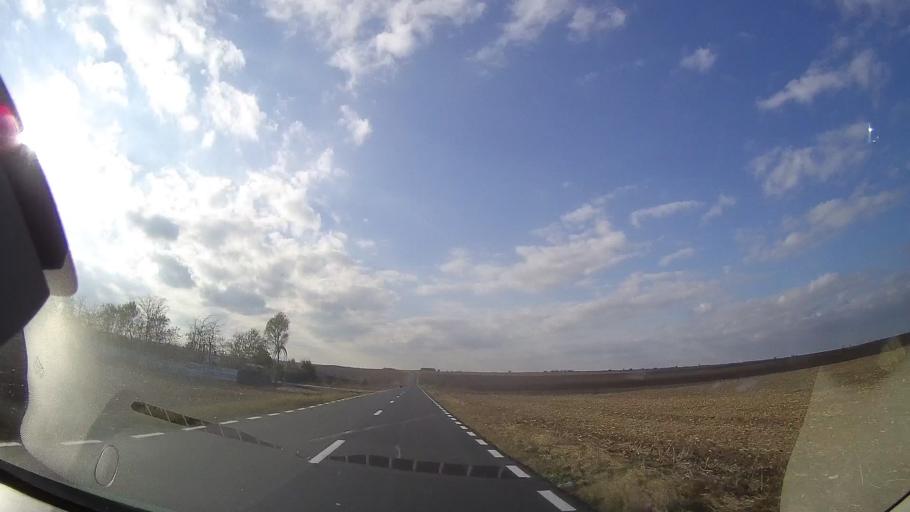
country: RO
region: Constanta
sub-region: Comuna Limanu
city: Limanu
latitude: 43.8245
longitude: 28.5045
